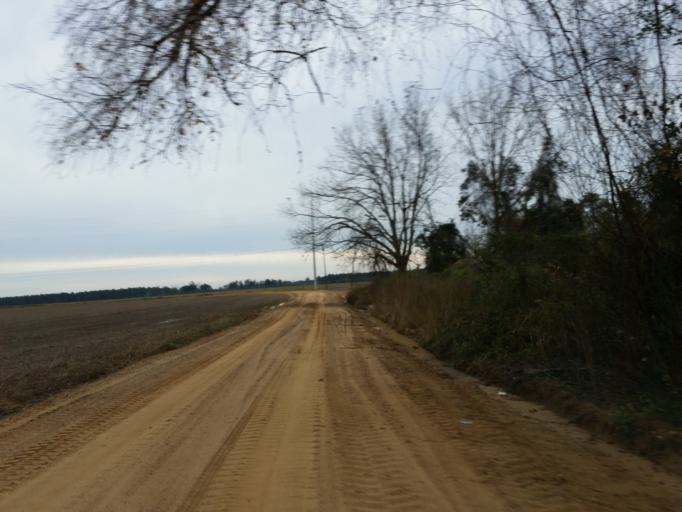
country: US
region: Georgia
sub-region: Dooly County
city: Vienna
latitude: 32.1463
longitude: -83.7711
